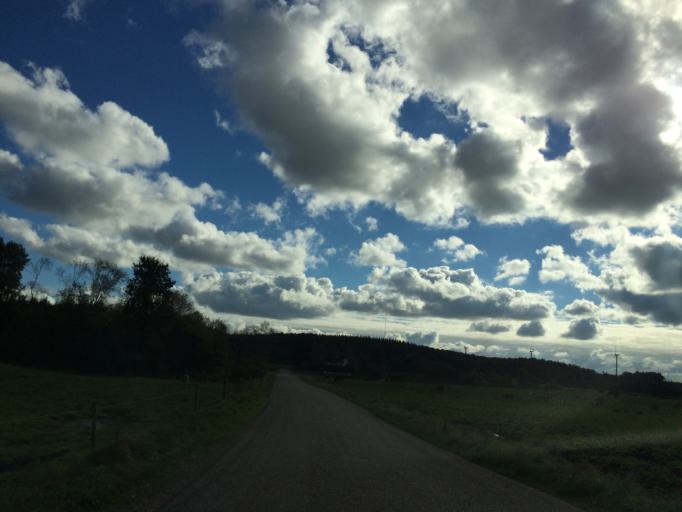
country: DK
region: Central Jutland
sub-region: Skanderborg Kommune
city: Ry
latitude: 56.1589
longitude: 9.7537
